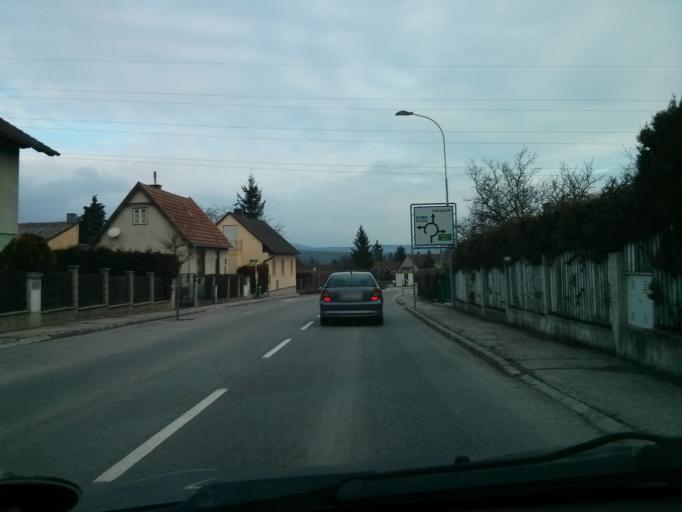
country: AT
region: Lower Austria
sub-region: Politischer Bezirk Baden
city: Hirtenberg
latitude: 47.9169
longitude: 16.1881
